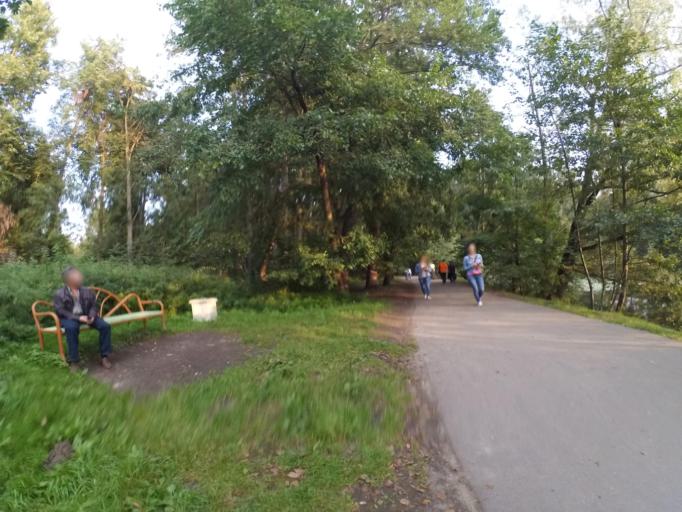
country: RU
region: Moscow
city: Kuz'minki
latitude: 55.6927
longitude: 37.7866
